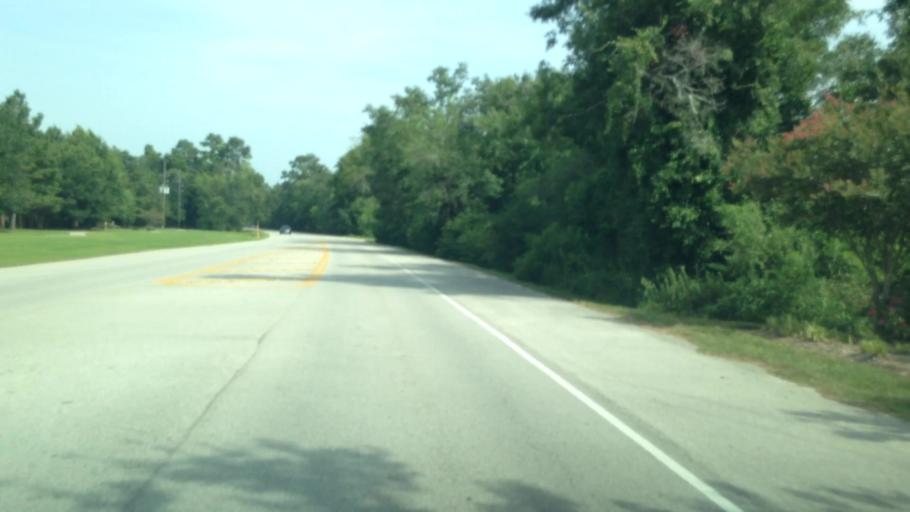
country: US
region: Texas
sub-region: Harris County
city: Atascocita
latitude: 29.9271
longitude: -95.1728
